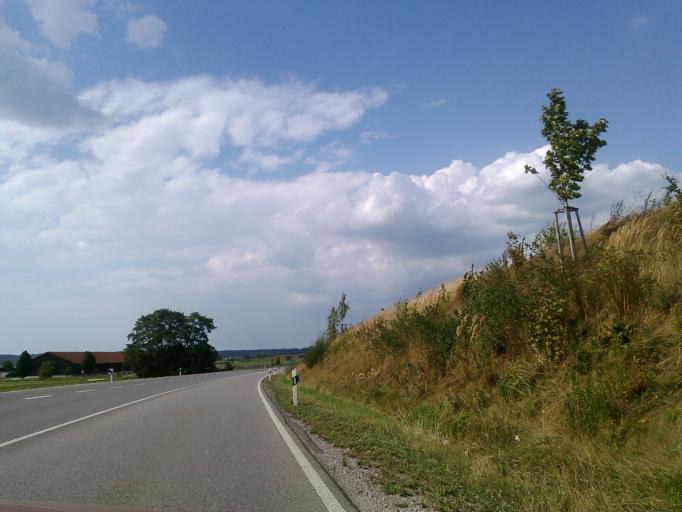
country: DE
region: Bavaria
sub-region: Upper Bavaria
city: Puchheim
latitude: 48.1462
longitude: 11.3411
